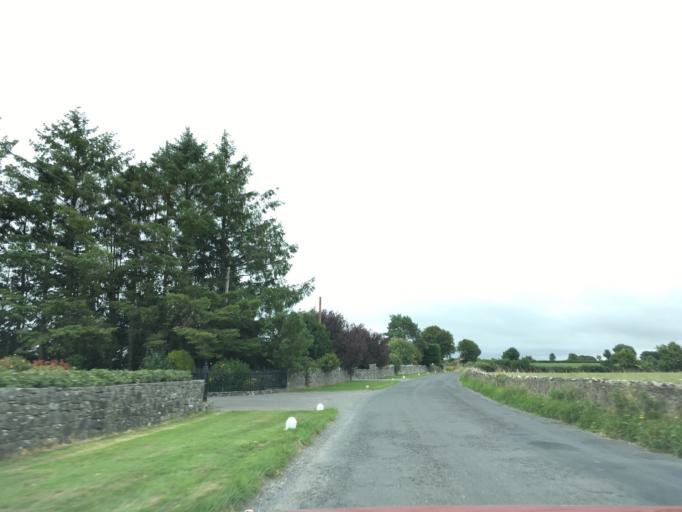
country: IE
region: Munster
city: Cashel
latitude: 52.4785
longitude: -7.8966
